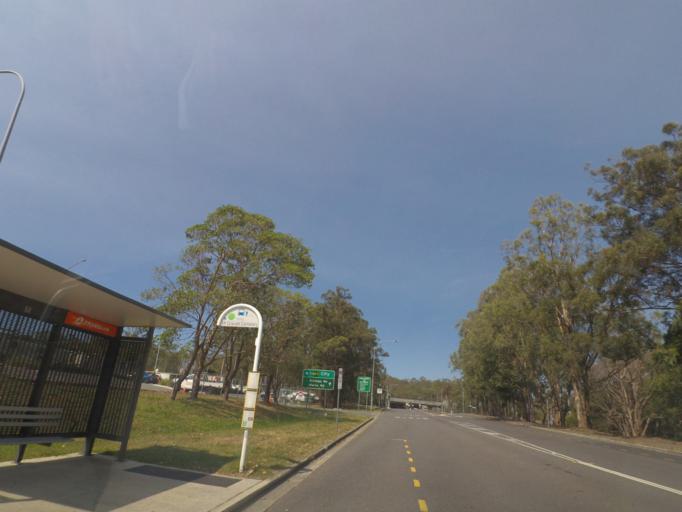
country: AU
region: Queensland
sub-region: Brisbane
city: Nathan
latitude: -27.5507
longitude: 153.0646
